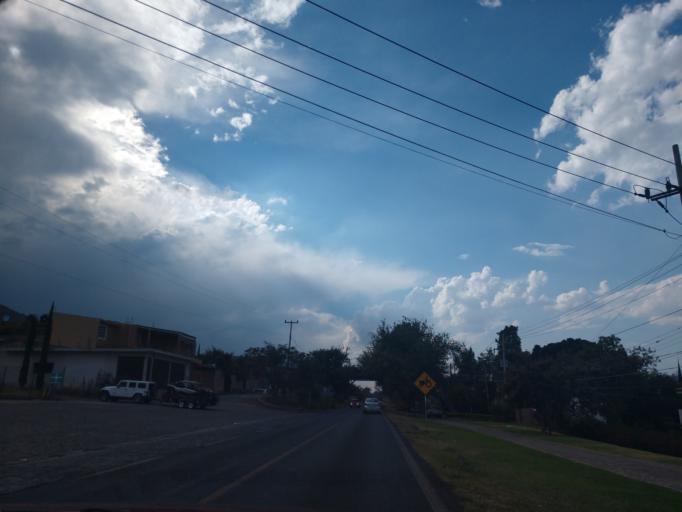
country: MX
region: Jalisco
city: San Juan Cosala
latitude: 20.2020
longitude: -103.3120
